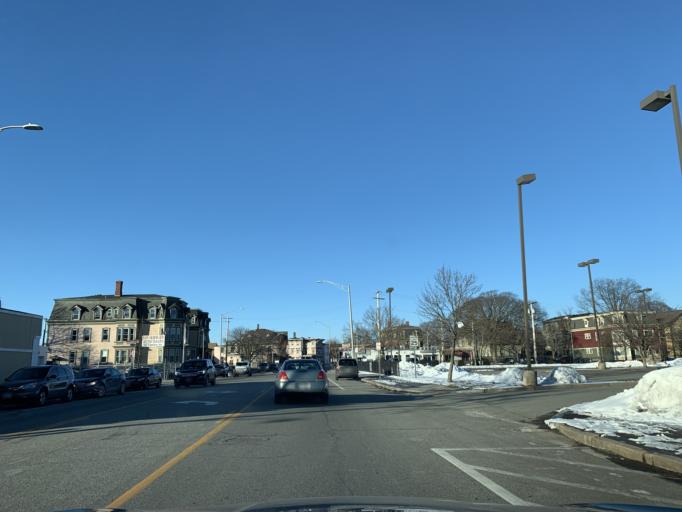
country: US
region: Rhode Island
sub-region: Providence County
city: Providence
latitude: 41.8077
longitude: -71.4247
